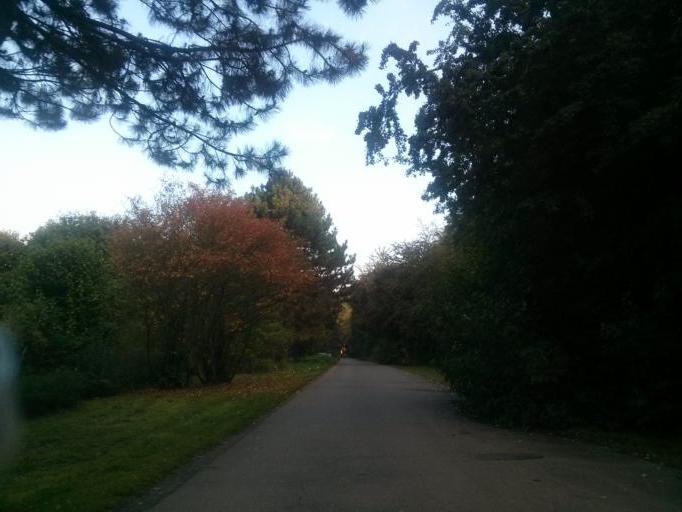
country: DE
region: North Rhine-Westphalia
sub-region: Regierungsbezirk Koln
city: Poll
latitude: 50.9030
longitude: 7.0009
